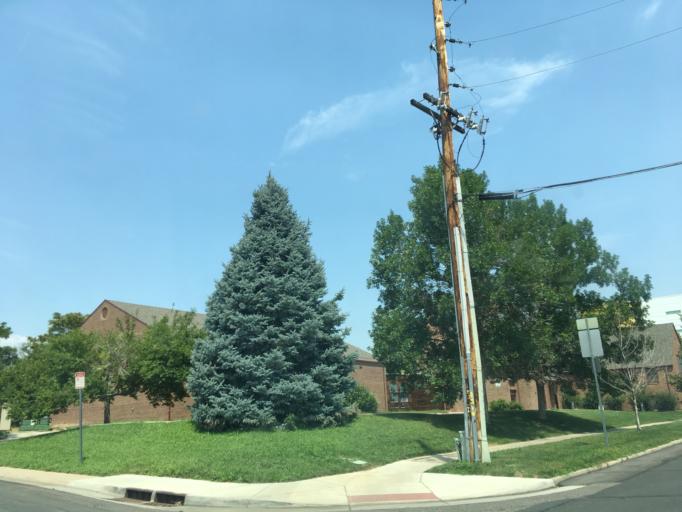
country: US
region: Colorado
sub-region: Jefferson County
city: Lakewood
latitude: 39.7094
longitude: -105.0299
